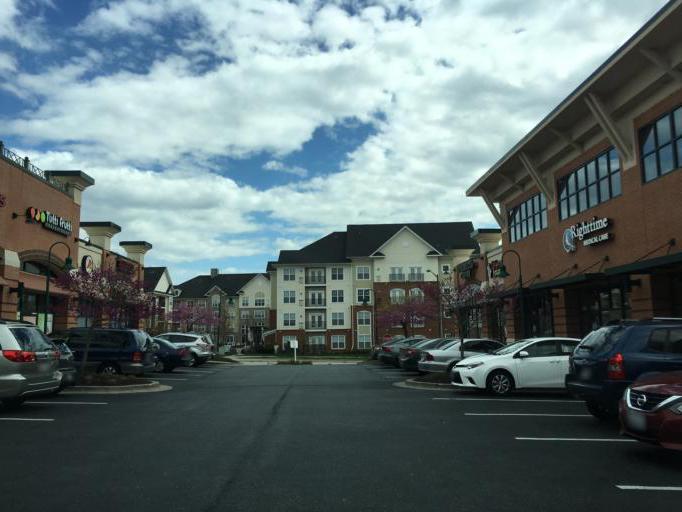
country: US
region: Maryland
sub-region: Anne Arundel County
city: Jessup
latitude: 39.1549
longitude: -76.7424
